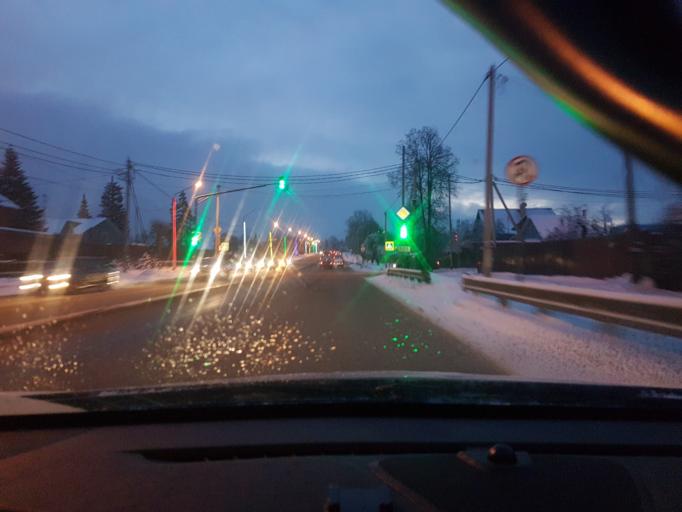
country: RU
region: Moskovskaya
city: Istra
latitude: 55.9080
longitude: 36.8806
